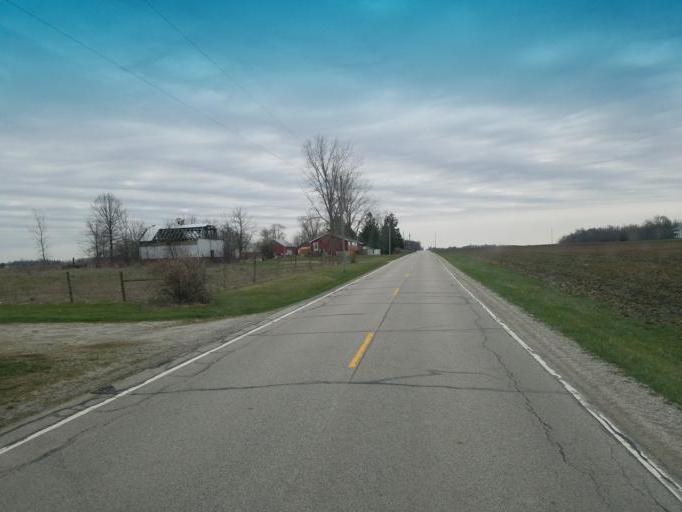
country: US
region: Ohio
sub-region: Crawford County
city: Bucyrus
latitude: 40.8631
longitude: -82.9401
